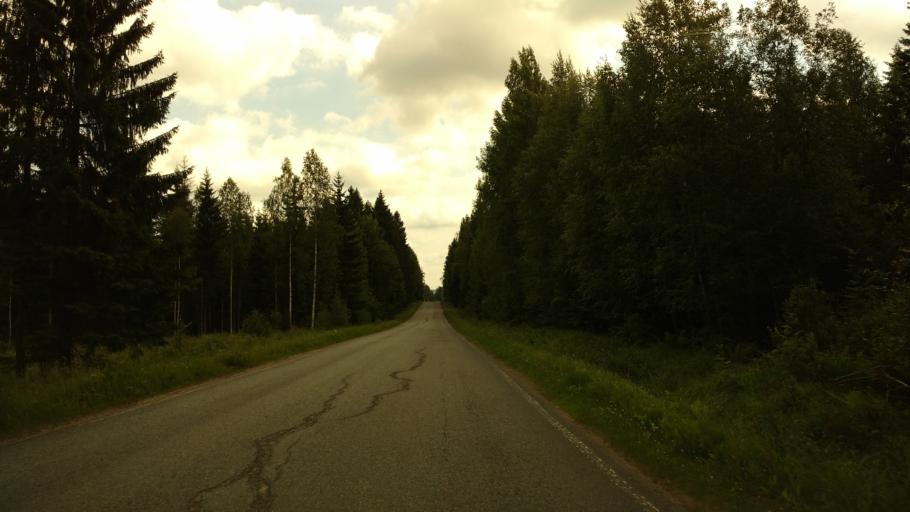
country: FI
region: Haeme
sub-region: Forssa
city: Ypaejae
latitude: 60.7758
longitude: 23.2559
